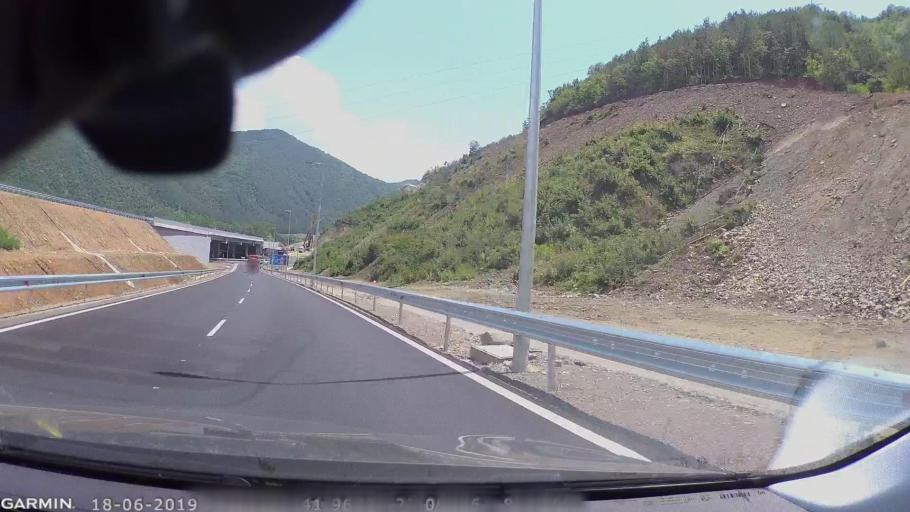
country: BG
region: Blagoevgrad
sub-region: Obshtina Blagoevgrad
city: Blagoevgrad
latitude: 41.9629
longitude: 23.0971
